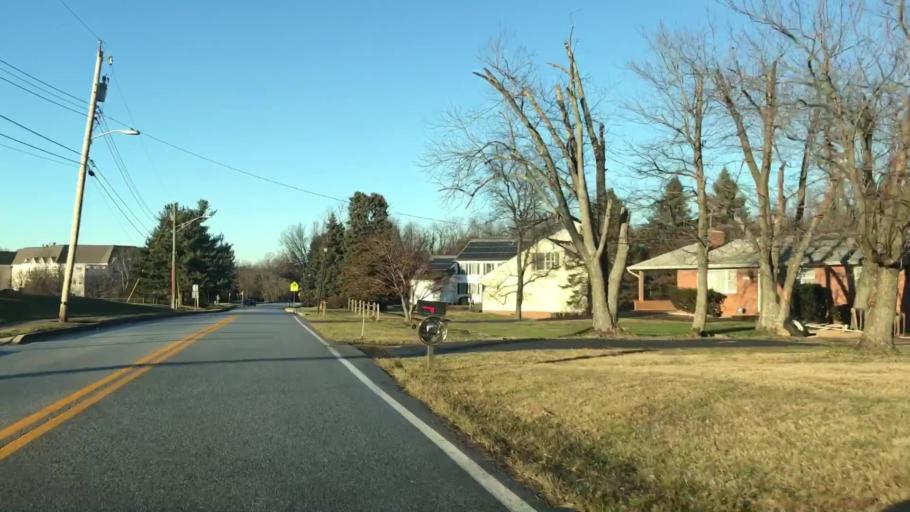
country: US
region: Maryland
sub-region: Howard County
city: Riverside
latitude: 39.1916
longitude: -76.8809
